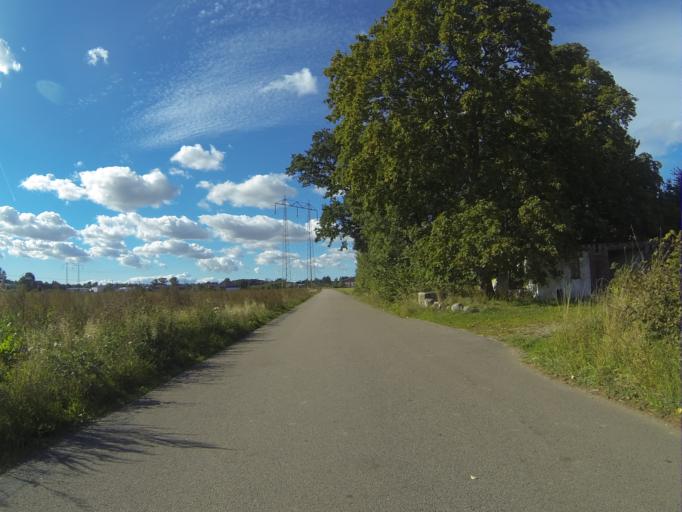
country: SE
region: Skane
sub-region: Lunds Kommun
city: Genarp
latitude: 55.7201
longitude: 13.3755
